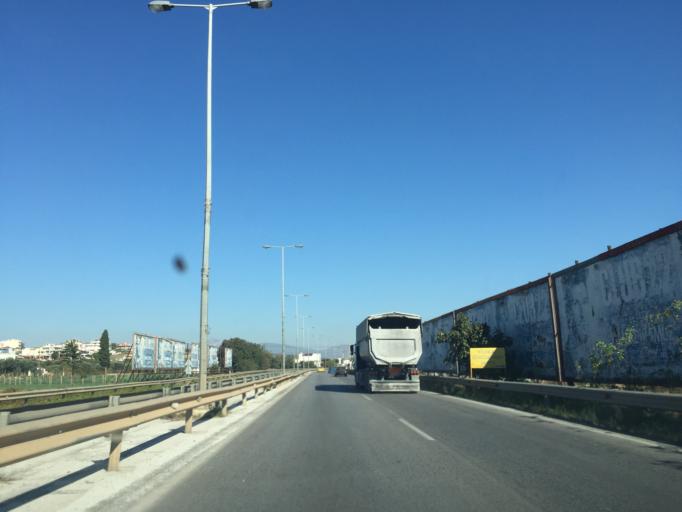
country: GR
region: Attica
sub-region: Nomarchia Anatolikis Attikis
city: Koropi
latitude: 37.8940
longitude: 23.8835
